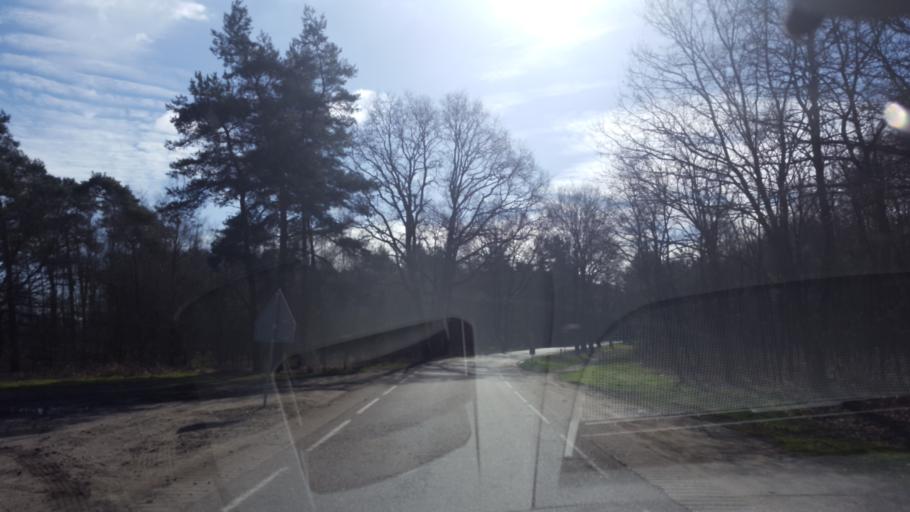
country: NL
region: Limburg
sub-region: Gemeente Weert
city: Weert
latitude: 51.2792
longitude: 5.6492
